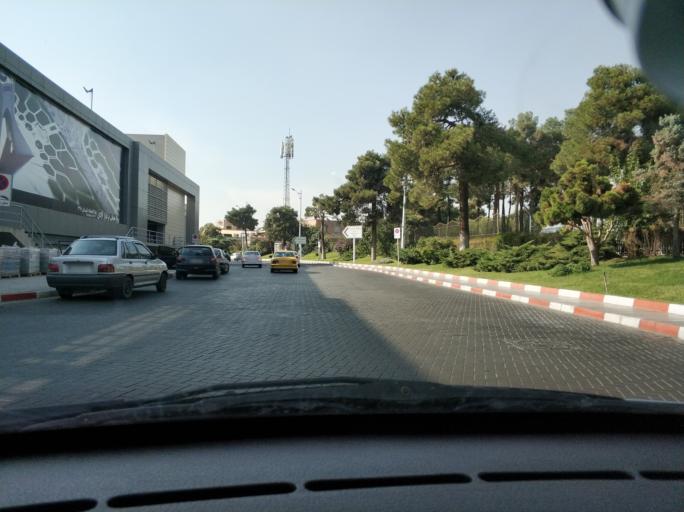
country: IR
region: Tehran
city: Tehran
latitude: 35.6934
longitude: 51.3233
